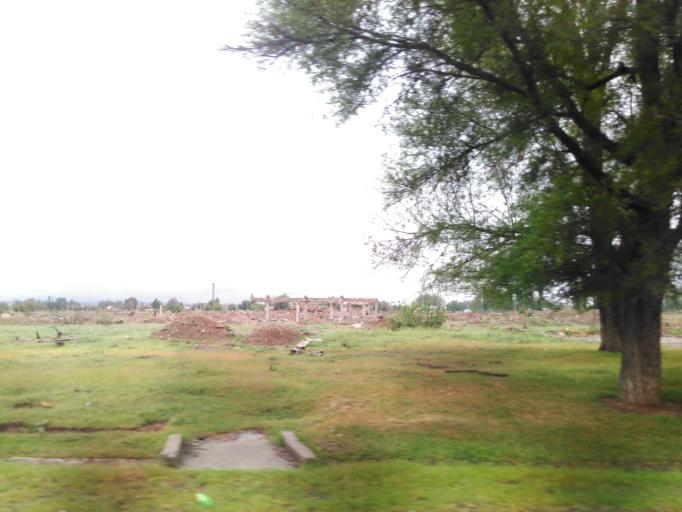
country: KG
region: Chuy
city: Tokmok
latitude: 42.8141
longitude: 75.3271
